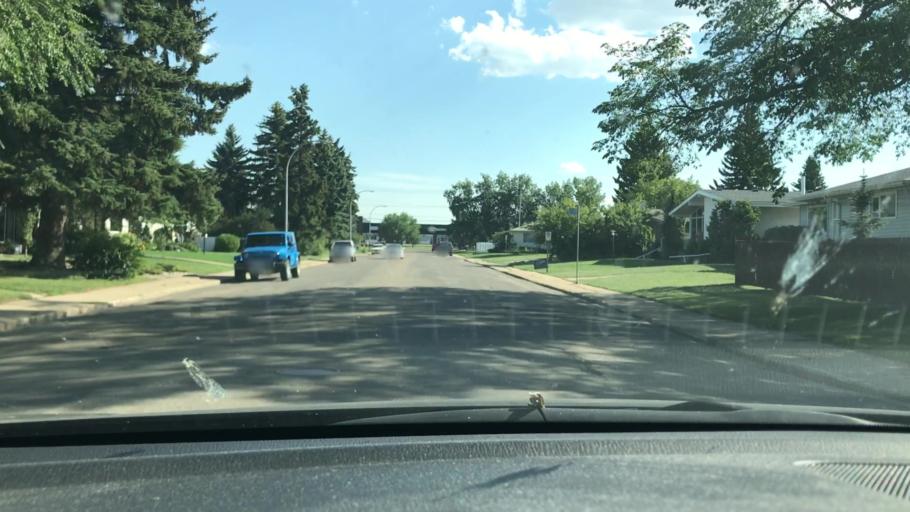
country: CA
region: Alberta
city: Edmonton
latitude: 53.5202
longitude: -113.4228
